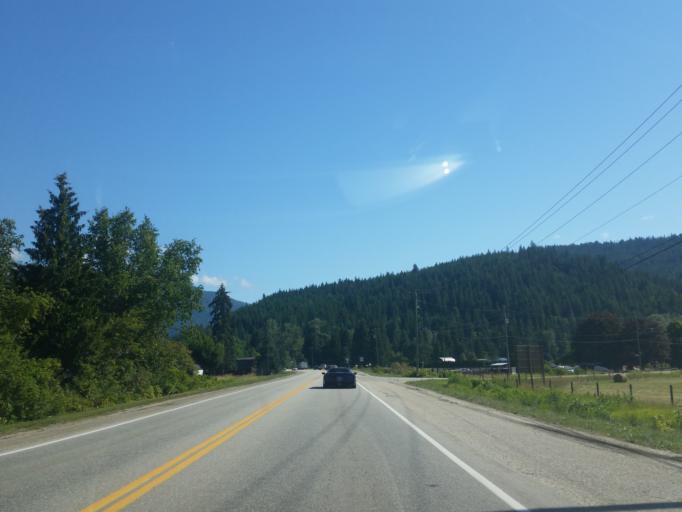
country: CA
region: British Columbia
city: Sicamous
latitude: 50.8483
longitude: -118.9500
